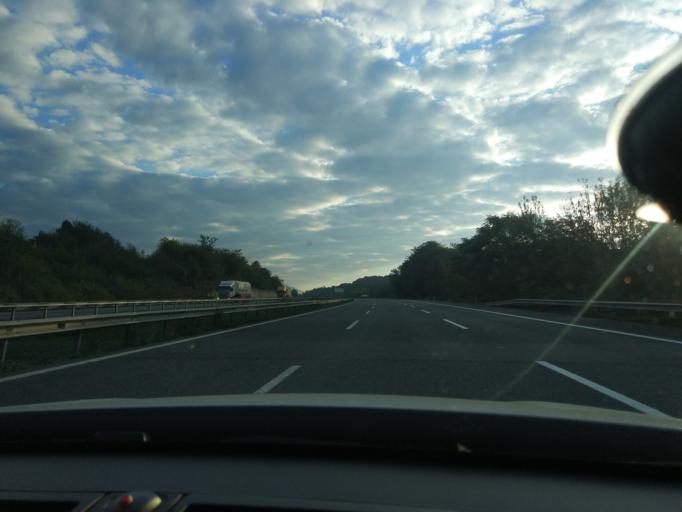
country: TR
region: Sakarya
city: Hendek
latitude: 40.7800
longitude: 30.7973
